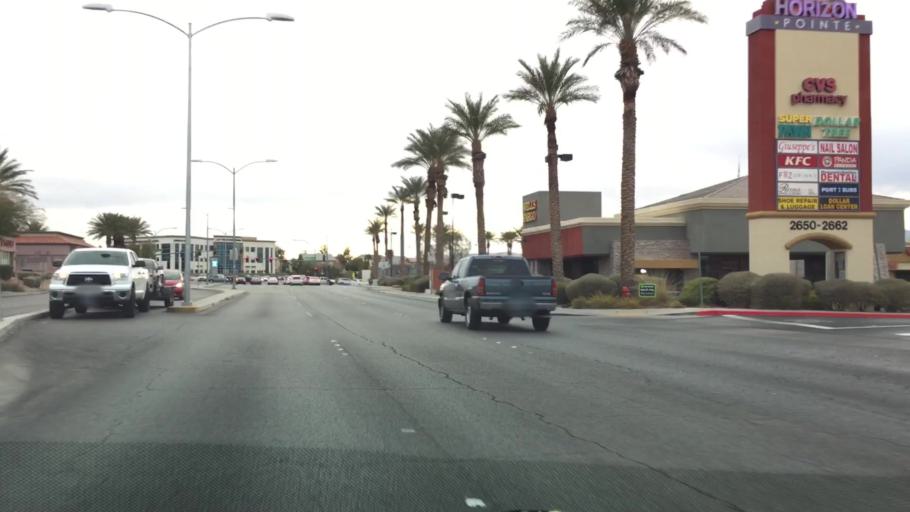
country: US
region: Nevada
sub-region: Clark County
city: Whitney
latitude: 36.0006
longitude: -115.1030
